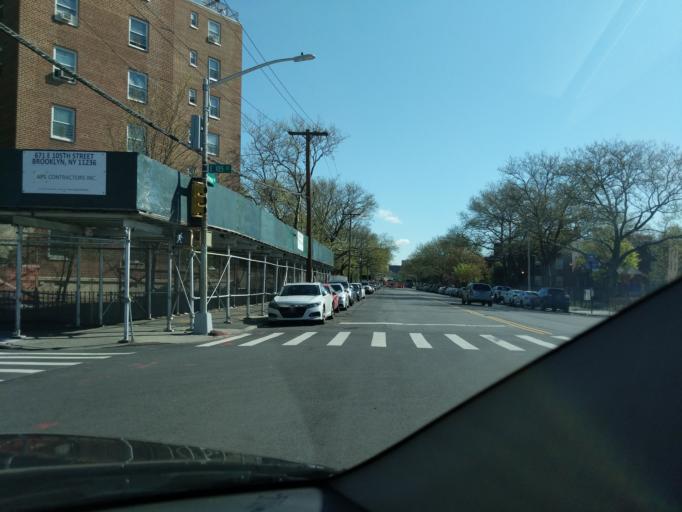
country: US
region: New York
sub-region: Kings County
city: East New York
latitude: 40.6490
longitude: -73.8963
